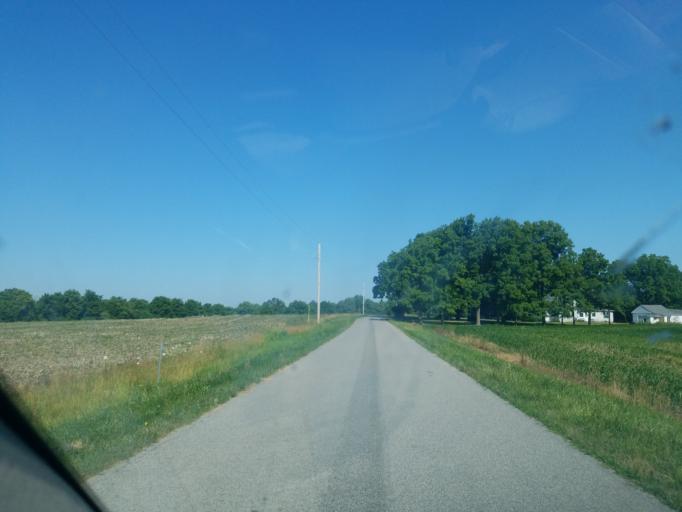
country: US
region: Ohio
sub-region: Logan County
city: Northwood
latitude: 40.4367
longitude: -83.6715
